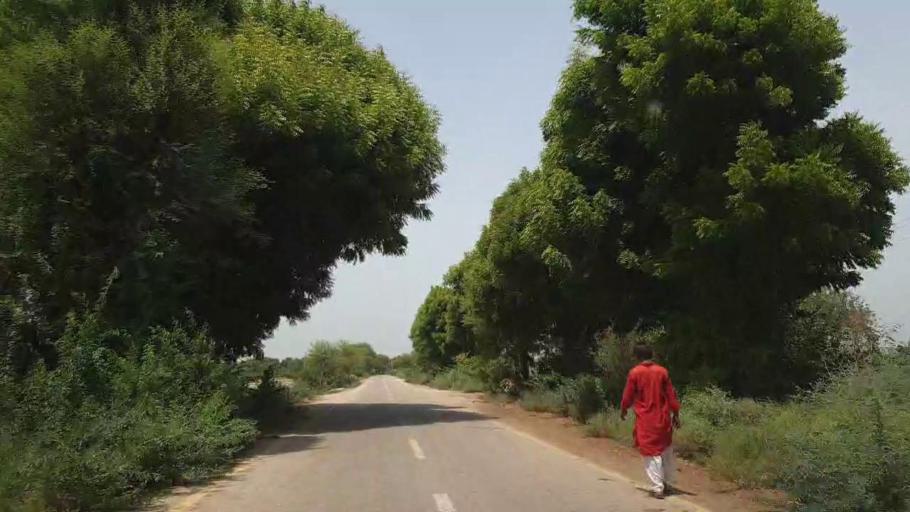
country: PK
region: Sindh
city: Sakrand
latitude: 26.2009
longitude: 68.2423
